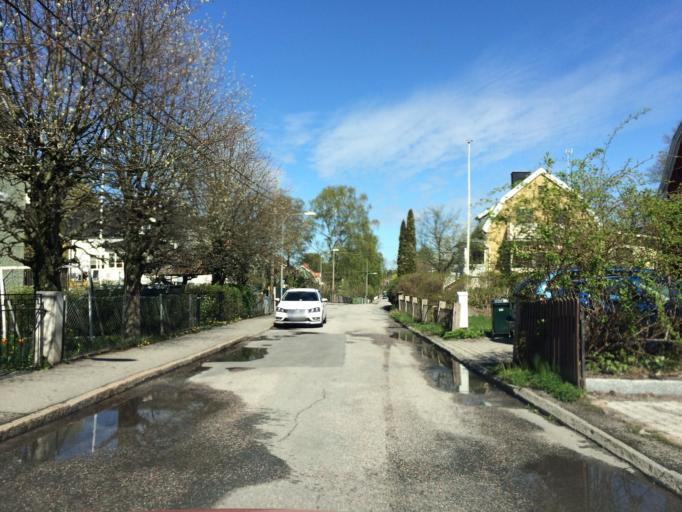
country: SE
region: Stockholm
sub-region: Huddinge Kommun
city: Segeltorp
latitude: 59.2976
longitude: 17.9639
